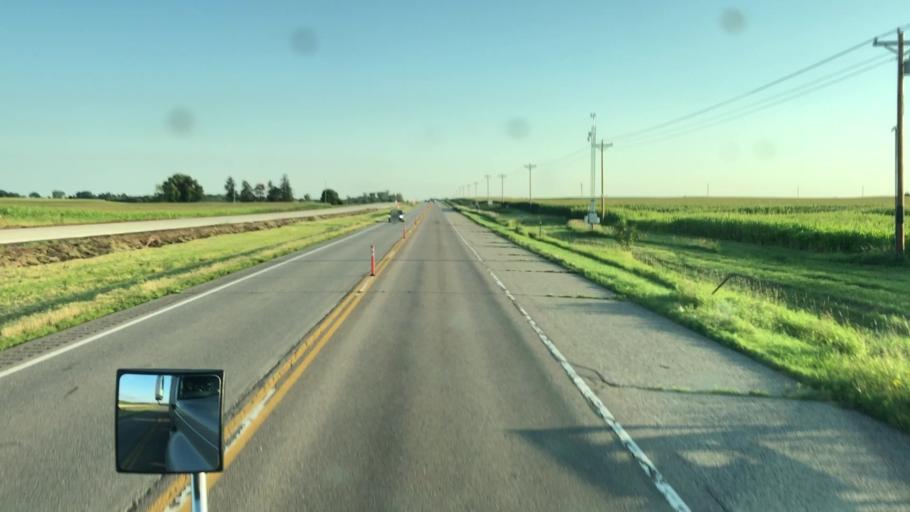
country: US
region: Minnesota
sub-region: Scott County
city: Belle Plaine
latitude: 44.5728
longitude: -93.8422
